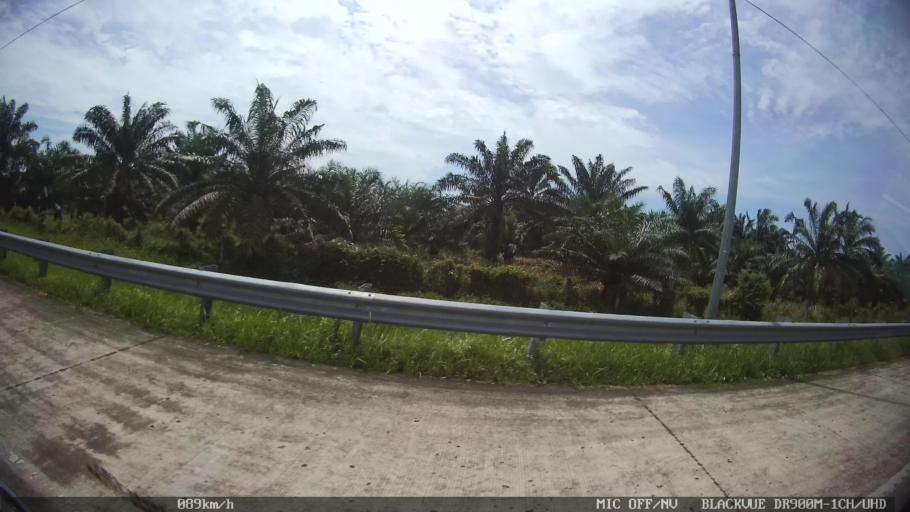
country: ID
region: North Sumatra
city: Percut
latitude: 3.6004
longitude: 98.8446
